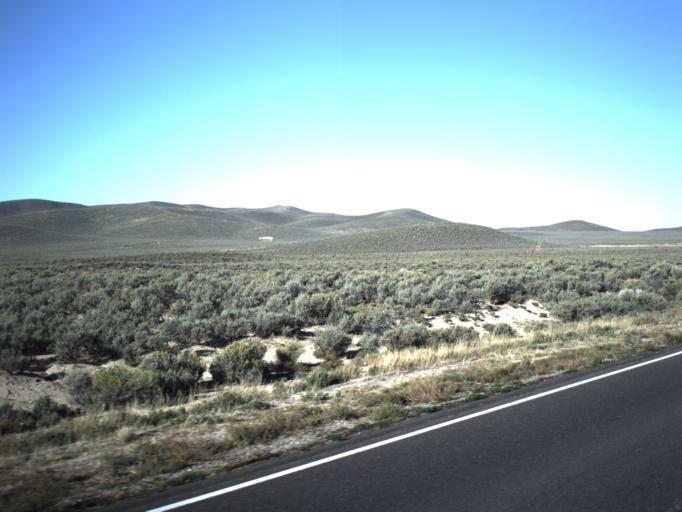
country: US
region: Utah
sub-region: Washington County
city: Enterprise
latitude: 37.7275
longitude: -113.7062
